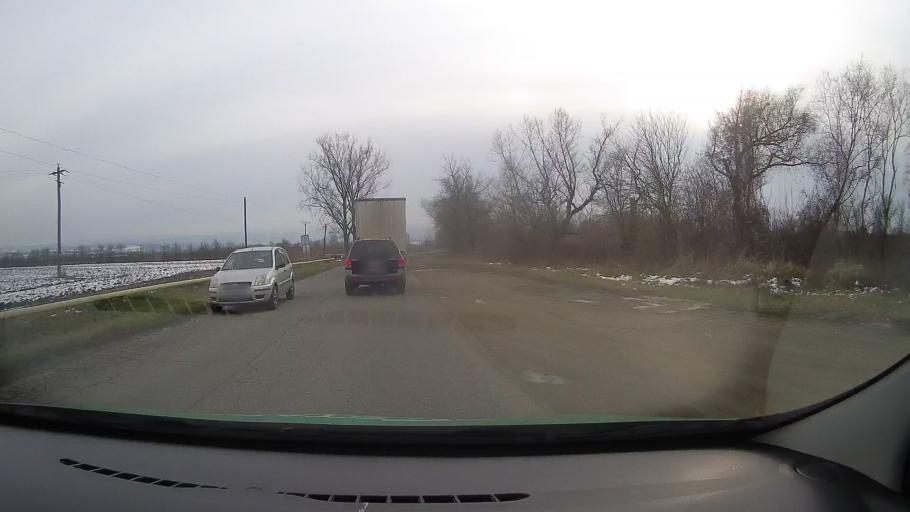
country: RO
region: Hunedoara
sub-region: Comuna Geoagiu
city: Geoagiu
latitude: 45.8975
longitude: 23.2257
